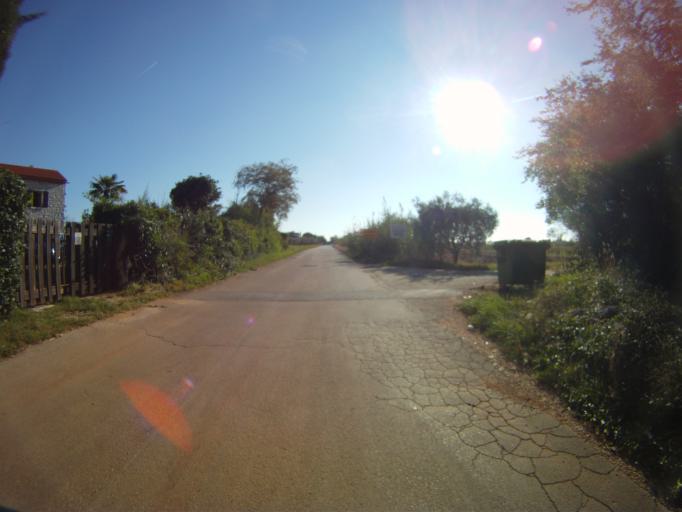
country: HR
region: Istarska
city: Umag
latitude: 45.3874
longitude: 13.5382
